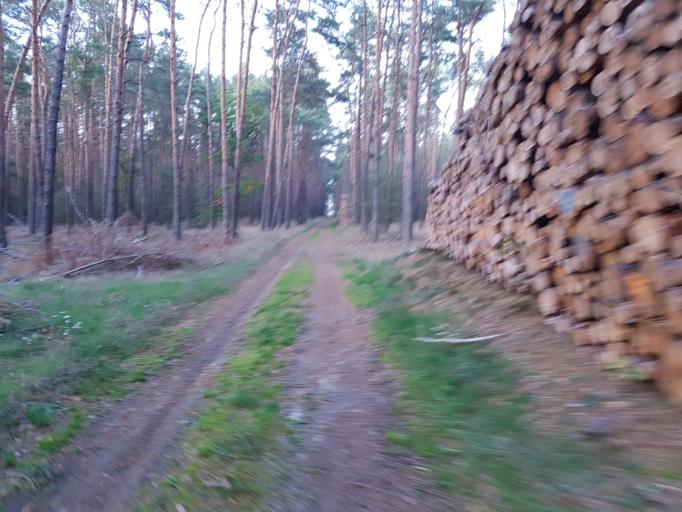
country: DE
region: Brandenburg
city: Bad Liebenwerda
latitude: 51.5399
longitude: 13.3817
